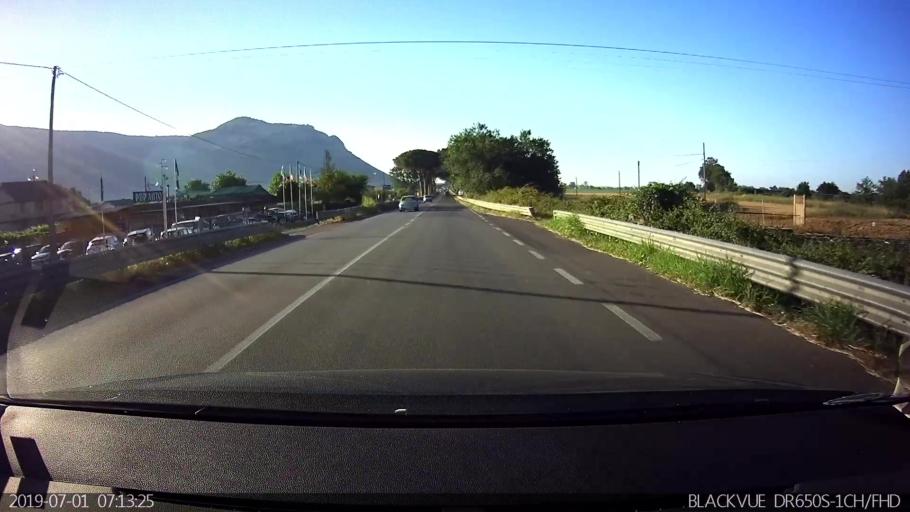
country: IT
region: Latium
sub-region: Provincia di Latina
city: Borgo Hermada
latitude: 41.3266
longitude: 13.1775
